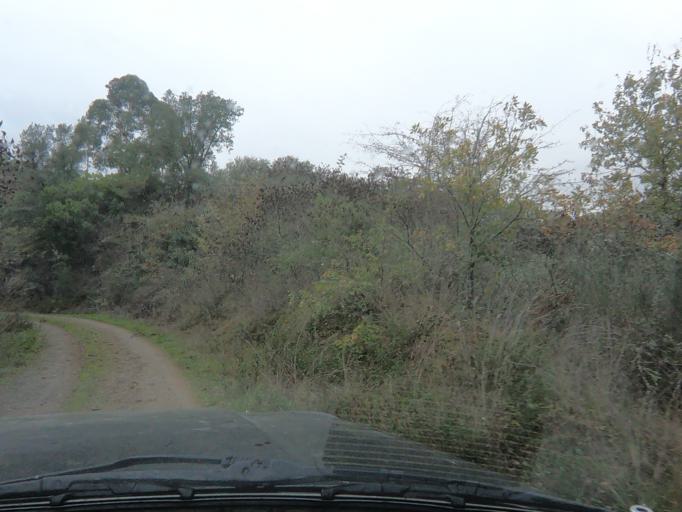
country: PT
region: Vila Real
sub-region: Santa Marta de Penaguiao
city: Santa Marta de Penaguiao
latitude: 41.2065
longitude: -7.7601
